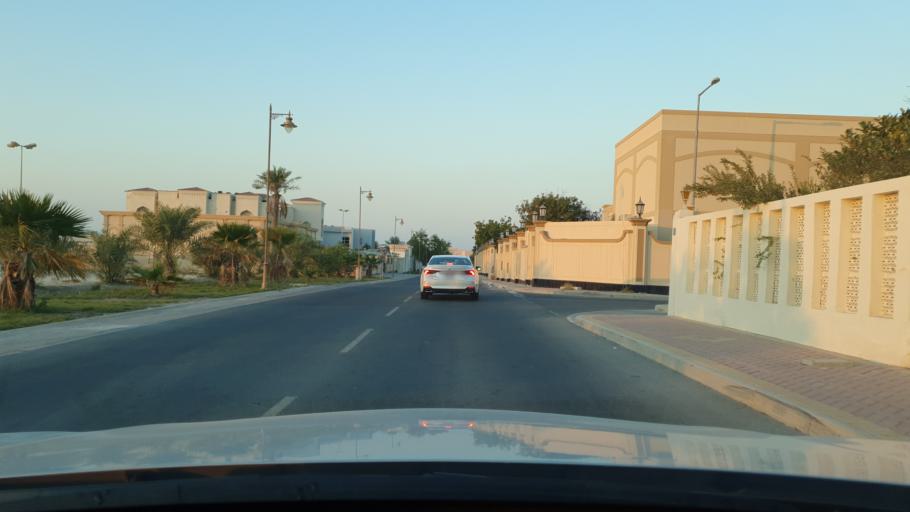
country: BH
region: Northern
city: Ar Rifa'
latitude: 26.1377
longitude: 50.5324
